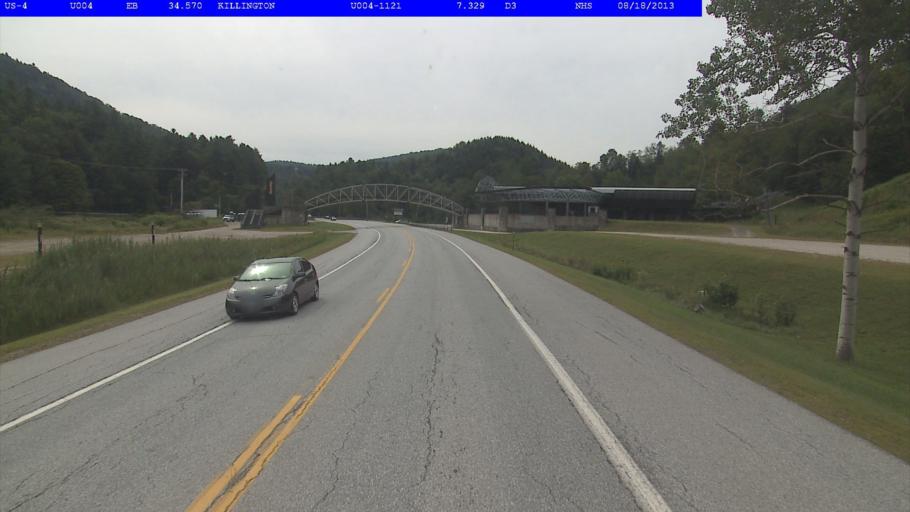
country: US
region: Vermont
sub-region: Rutland County
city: Rutland
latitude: 43.6156
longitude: -72.7570
